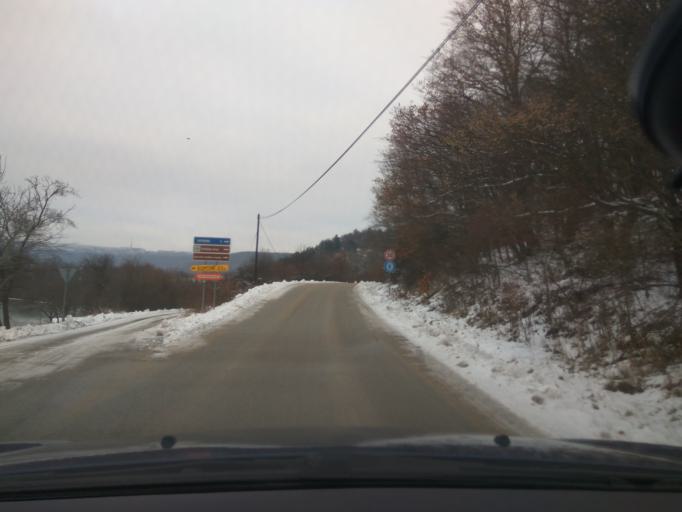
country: SK
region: Nitriansky
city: Stara Tura
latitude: 48.8221
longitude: 17.7034
